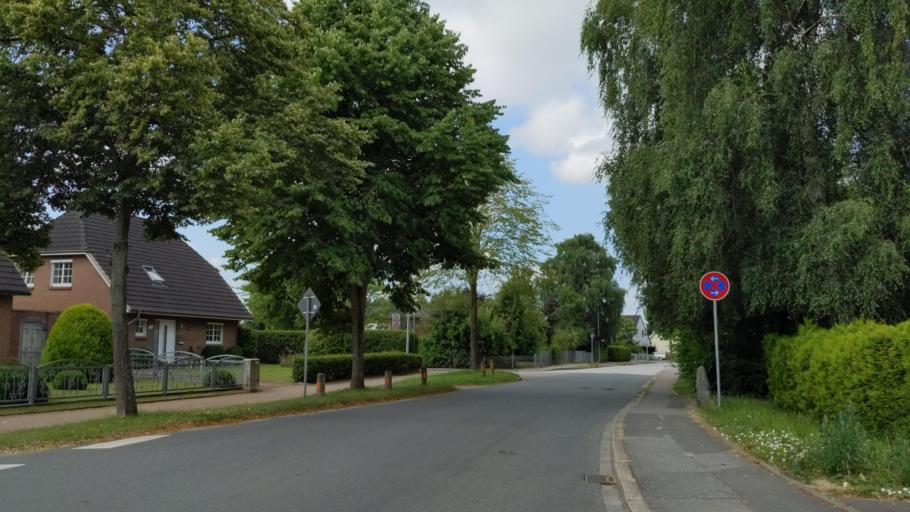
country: DE
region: Schleswig-Holstein
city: Stockelsdorf
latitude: 53.8915
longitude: 10.6313
